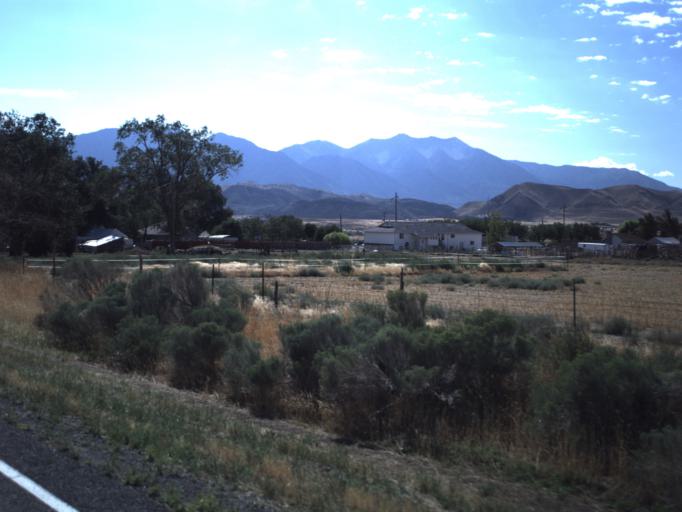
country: US
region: Utah
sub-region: Utah County
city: Genola
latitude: 39.9519
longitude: -111.9586
